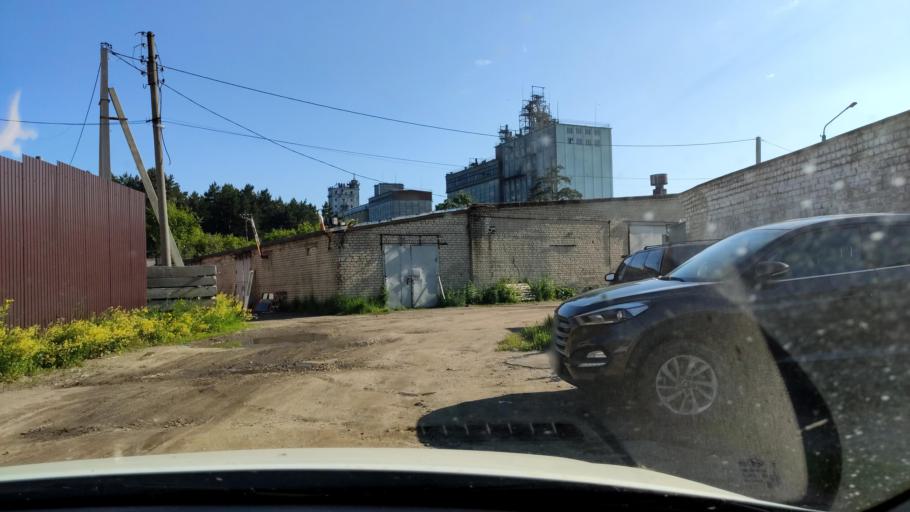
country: RU
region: Tatarstan
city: Staroye Arakchino
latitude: 55.8416
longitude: 49.0448
